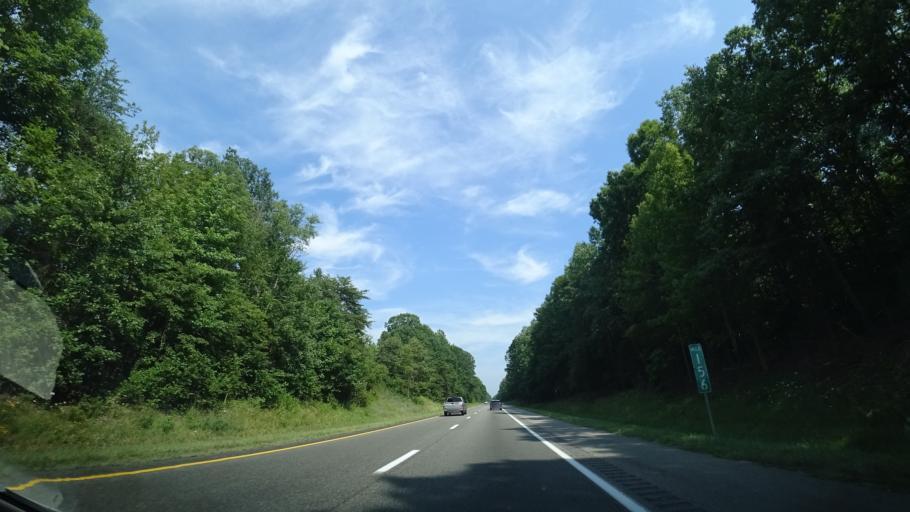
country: US
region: Virginia
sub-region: Goochland County
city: Goochland
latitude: 37.8136
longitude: -77.9400
